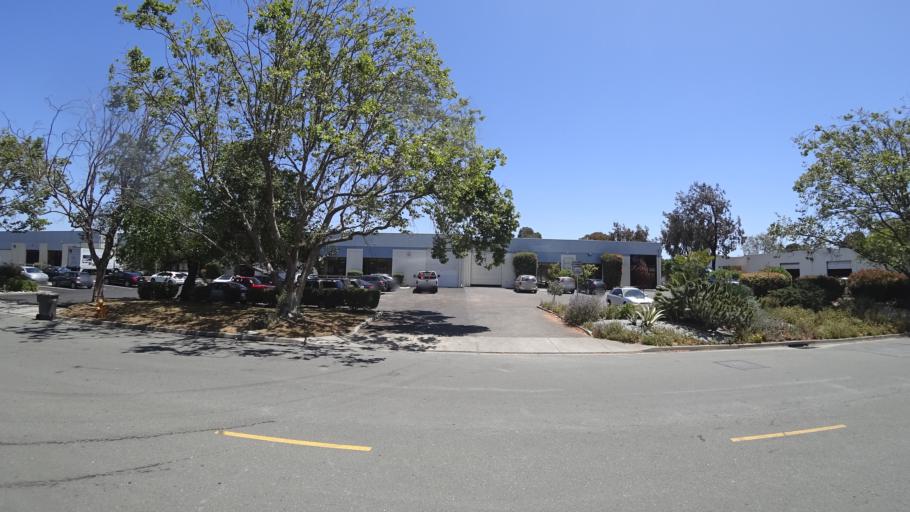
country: US
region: California
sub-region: Alameda County
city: San Lorenzo
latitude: 37.6369
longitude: -122.1249
